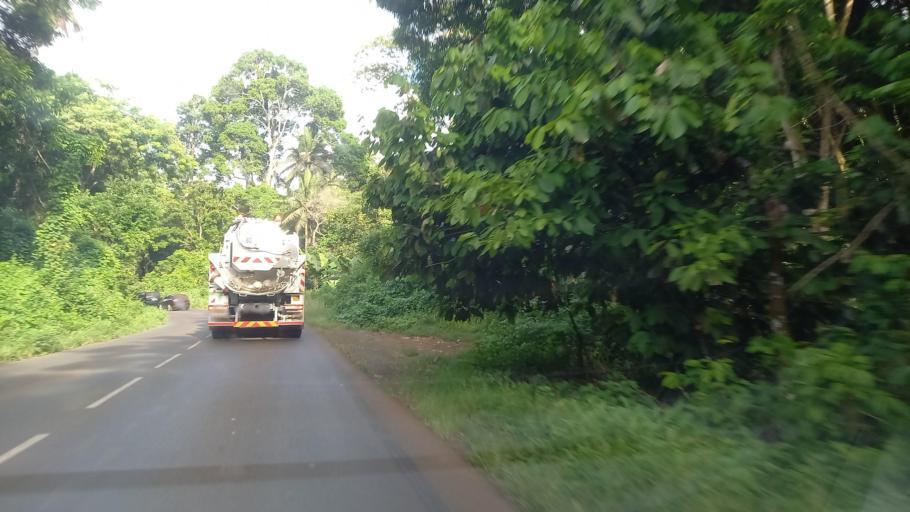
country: YT
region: Chiconi
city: Chiconi
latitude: -12.8162
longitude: 45.1294
